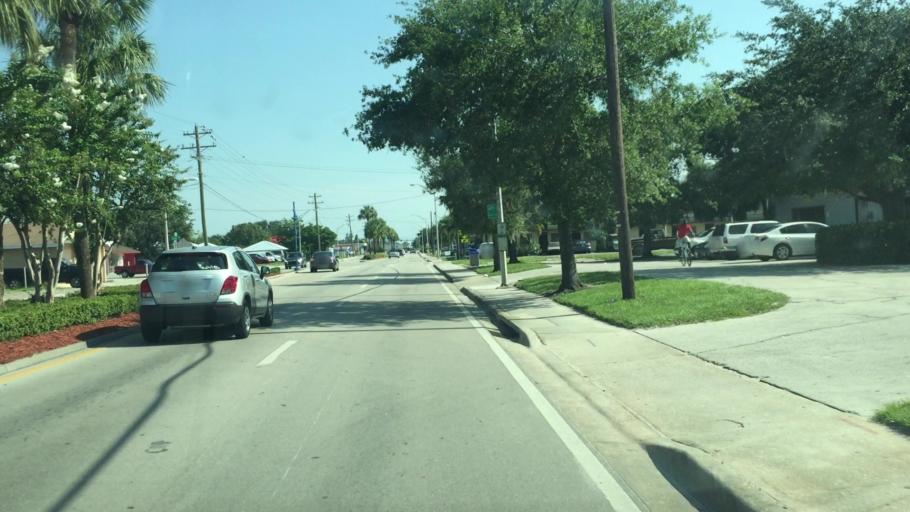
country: US
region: Florida
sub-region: Collier County
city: Immokalee
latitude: 26.4141
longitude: -81.4172
